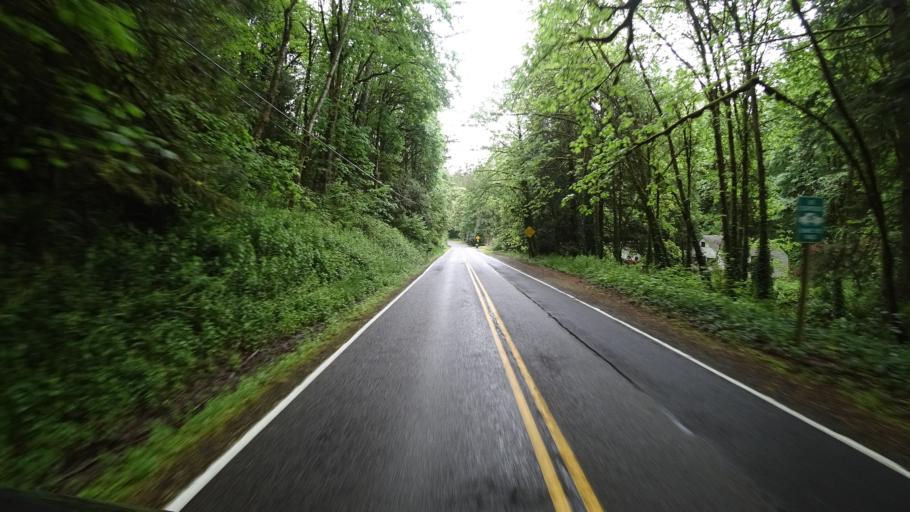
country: US
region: Oregon
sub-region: Washington County
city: West Haven-Sylvan
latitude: 45.5361
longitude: -122.7403
